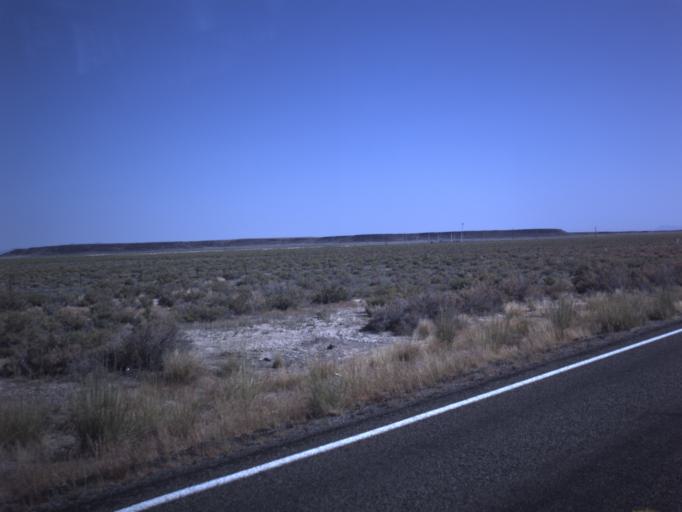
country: US
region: Utah
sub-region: Millard County
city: Delta
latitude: 39.1334
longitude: -112.7296
